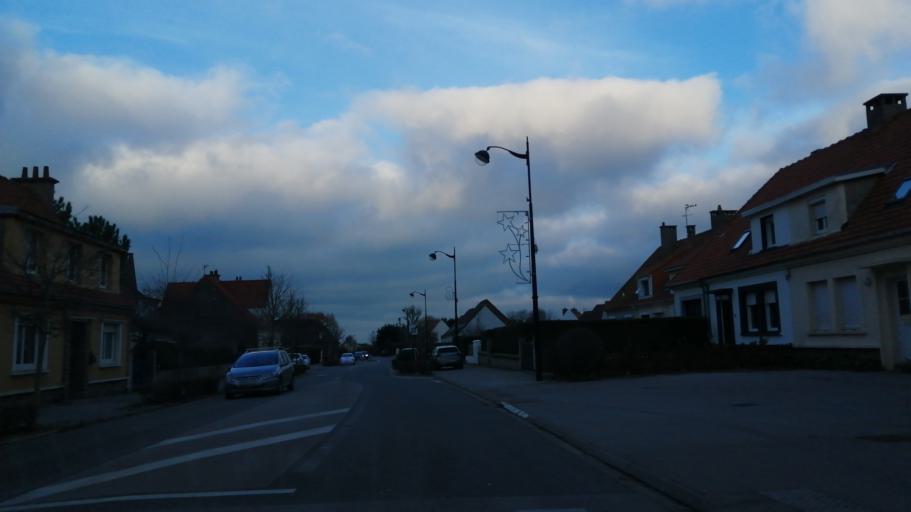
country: FR
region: Nord-Pas-de-Calais
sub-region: Departement du Pas-de-Calais
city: Ambleteuse
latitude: 50.8523
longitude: 1.6129
